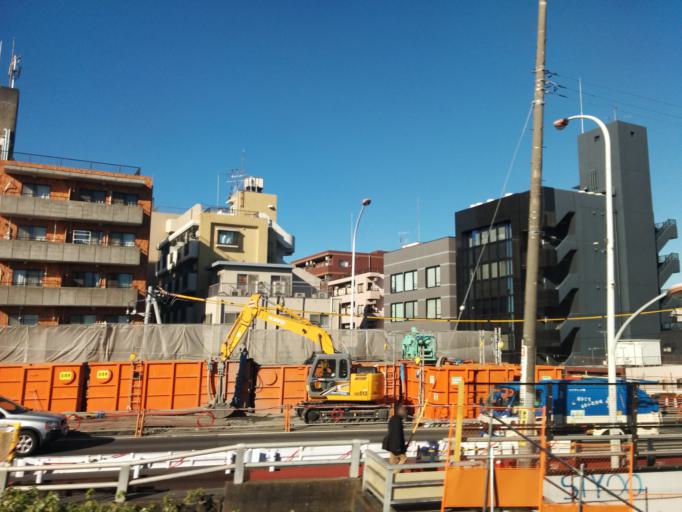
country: JP
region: Kanagawa
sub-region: Kawasaki-shi
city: Kawasaki
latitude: 35.5767
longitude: 139.6631
